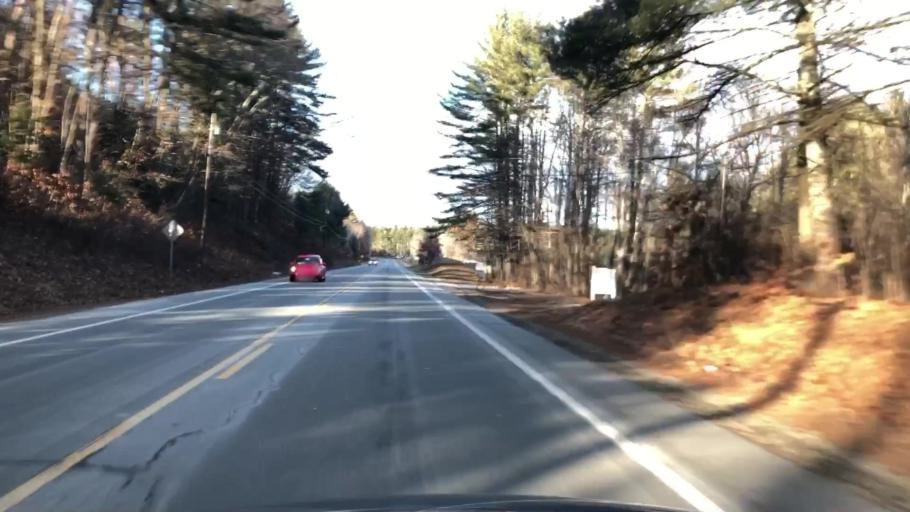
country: US
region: New Hampshire
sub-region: Hillsborough County
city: Brookline
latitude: 42.7182
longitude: -71.6624
